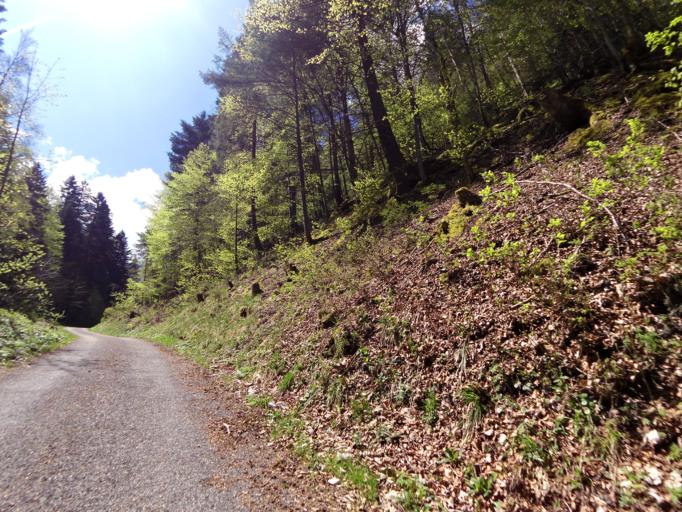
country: CH
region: Vaud
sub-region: Jura-Nord vaudois District
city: L'Abbaye
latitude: 46.6872
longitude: 6.3421
